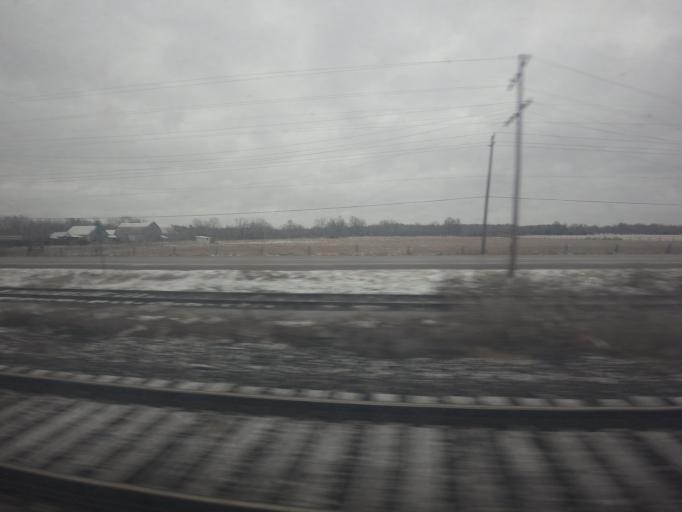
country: CA
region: Ontario
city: Gananoque
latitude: 44.3682
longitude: -76.1595
